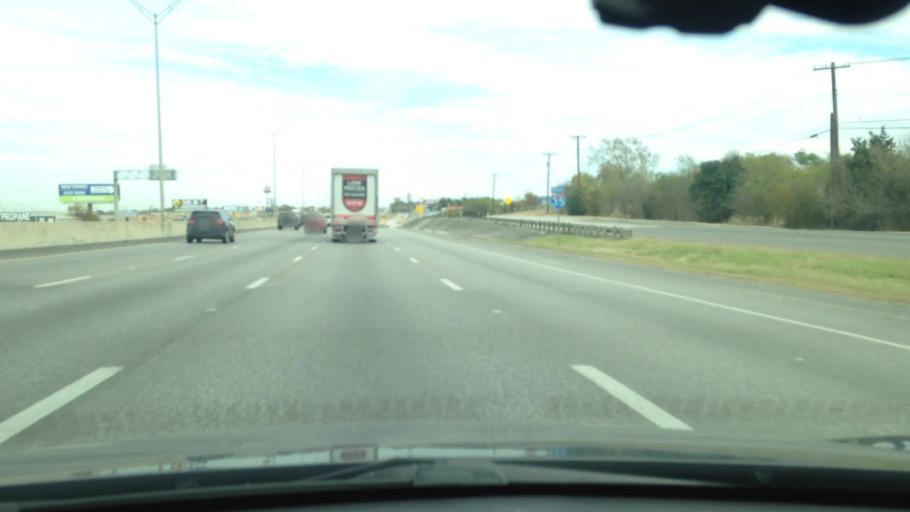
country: US
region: Texas
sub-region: Comal County
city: New Braunfels
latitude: 29.6683
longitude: -98.1625
